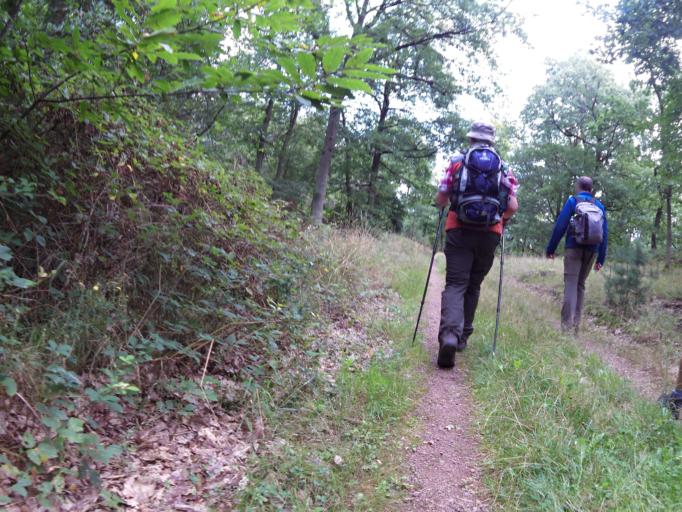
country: DE
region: Rheinland-Pfalz
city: Bad Munster am Stein-Ebernburg
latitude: 49.8260
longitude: 7.8375
